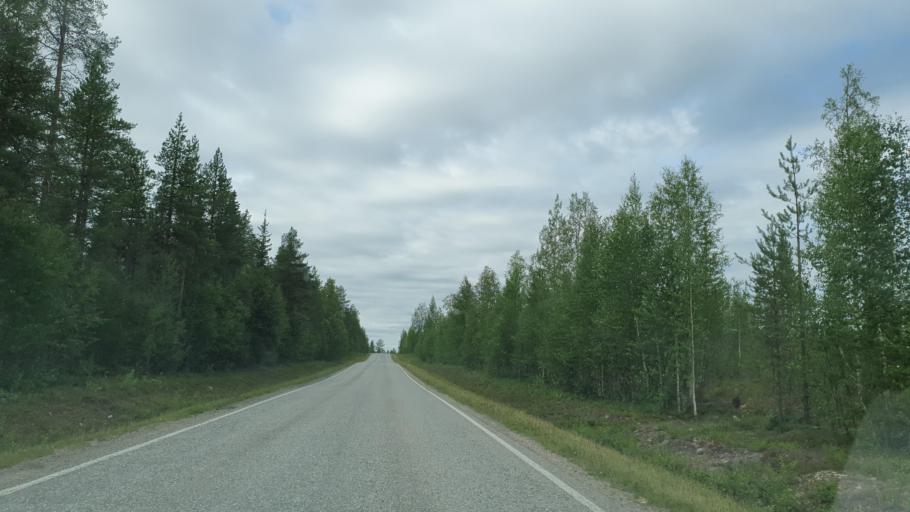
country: FI
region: Lapland
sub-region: Tunturi-Lappi
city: Kittilae
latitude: 67.6111
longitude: 25.2393
